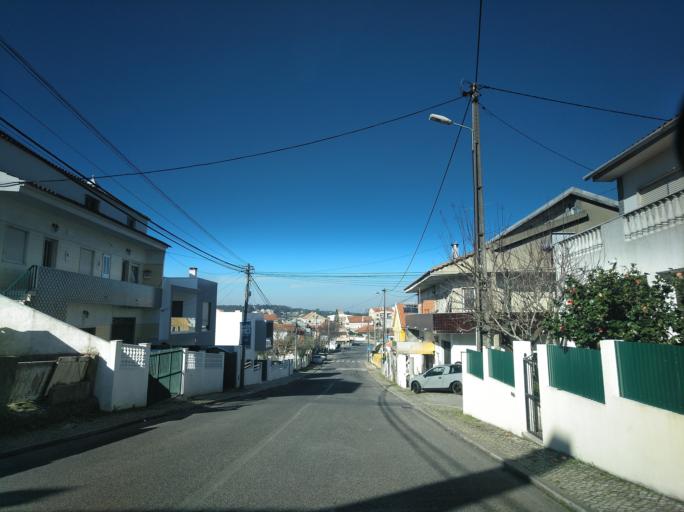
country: PT
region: Lisbon
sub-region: Odivelas
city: Canecas
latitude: 38.8051
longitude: -9.2194
